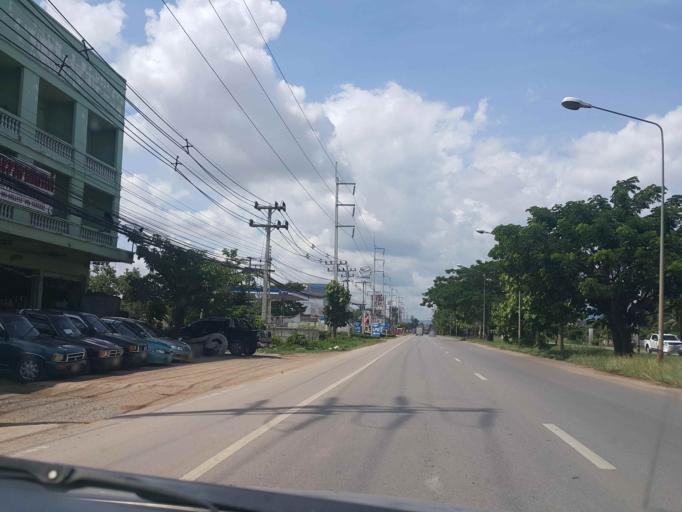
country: TH
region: Phayao
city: Phayao
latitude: 19.1528
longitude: 99.9130
